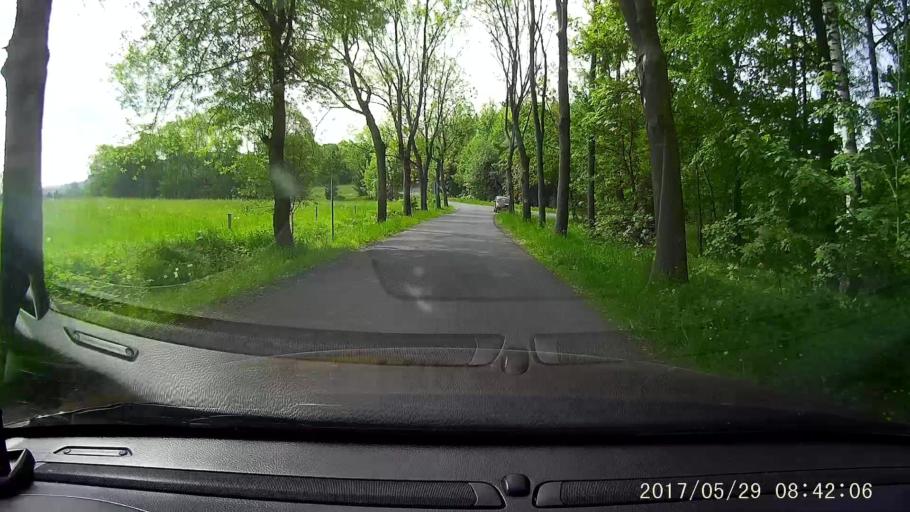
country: PL
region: Lower Silesian Voivodeship
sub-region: Powiat zlotoryjski
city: Swierzawa
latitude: 50.9682
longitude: 15.8277
